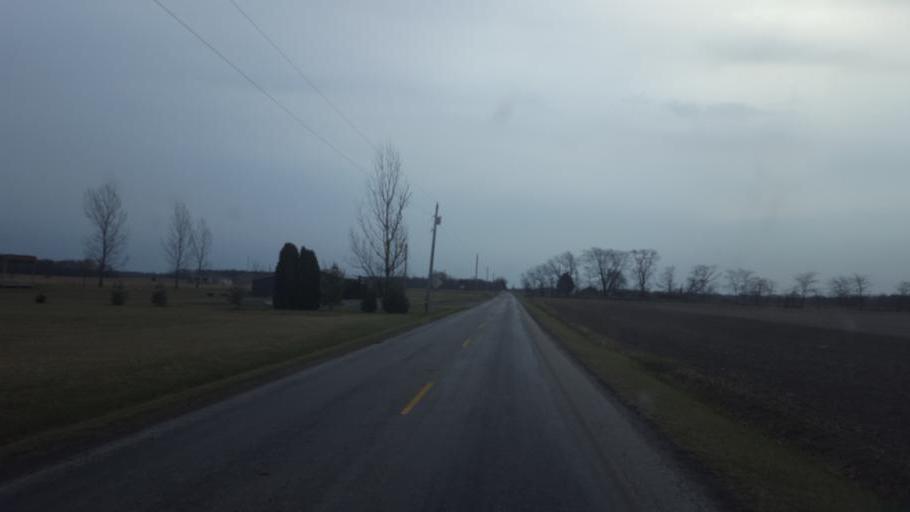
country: US
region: Ohio
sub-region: Marion County
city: Marion
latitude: 40.6523
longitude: -82.9895
